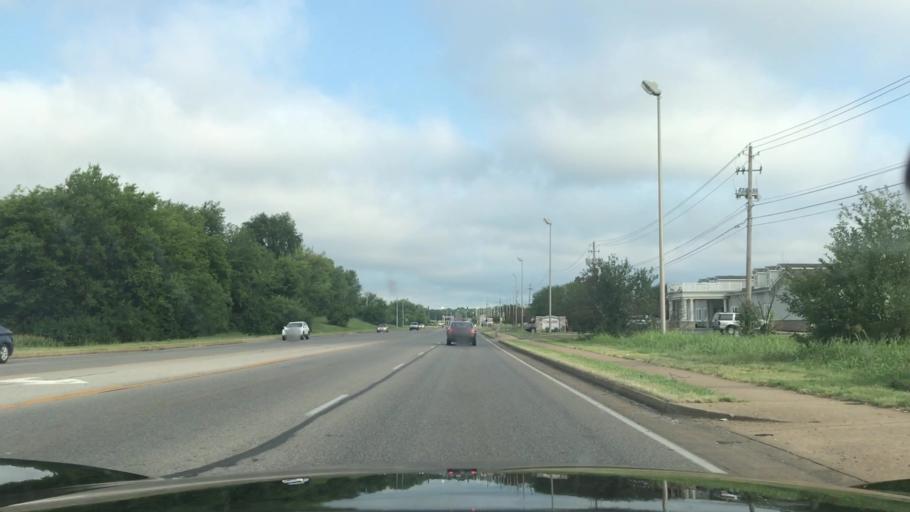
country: US
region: Kentucky
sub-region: Warren County
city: Bowling Green
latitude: 36.9555
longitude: -86.4457
